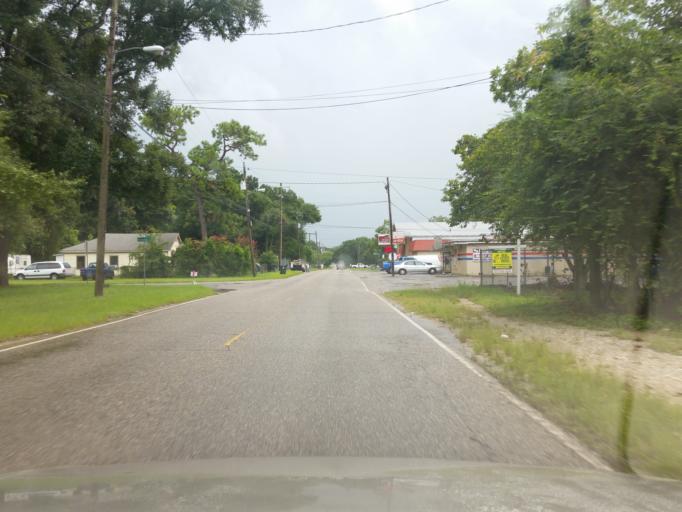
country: US
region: Florida
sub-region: Escambia County
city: Brent
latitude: 30.4568
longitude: -87.2456
